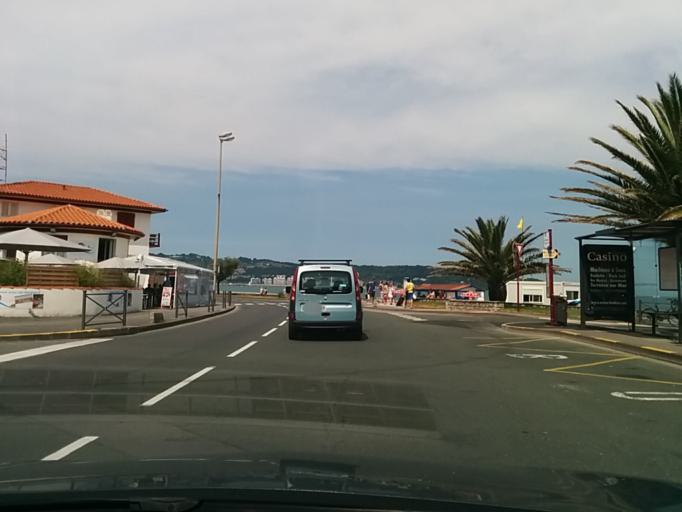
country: FR
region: Aquitaine
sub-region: Departement des Pyrenees-Atlantiques
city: Hendaye
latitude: 43.3755
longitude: -1.7620
